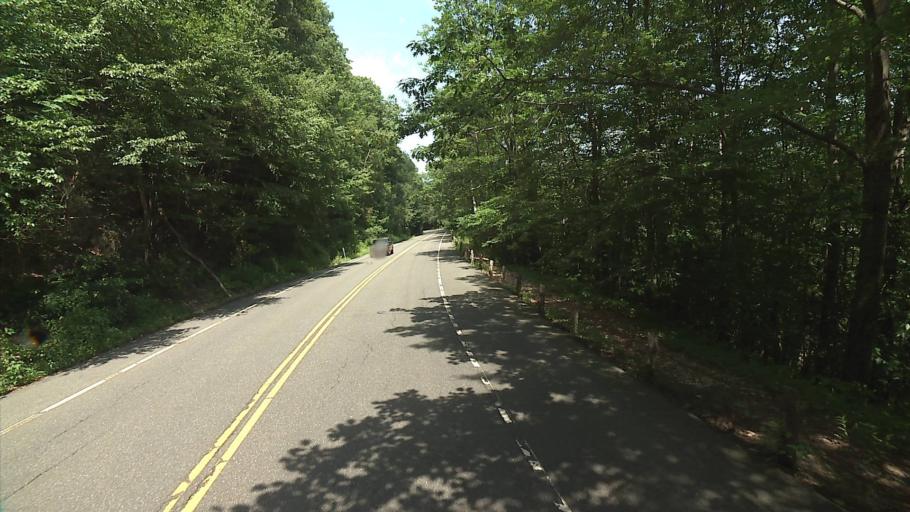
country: US
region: Massachusetts
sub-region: Hampden County
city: Granville
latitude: 42.0225
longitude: -72.9450
